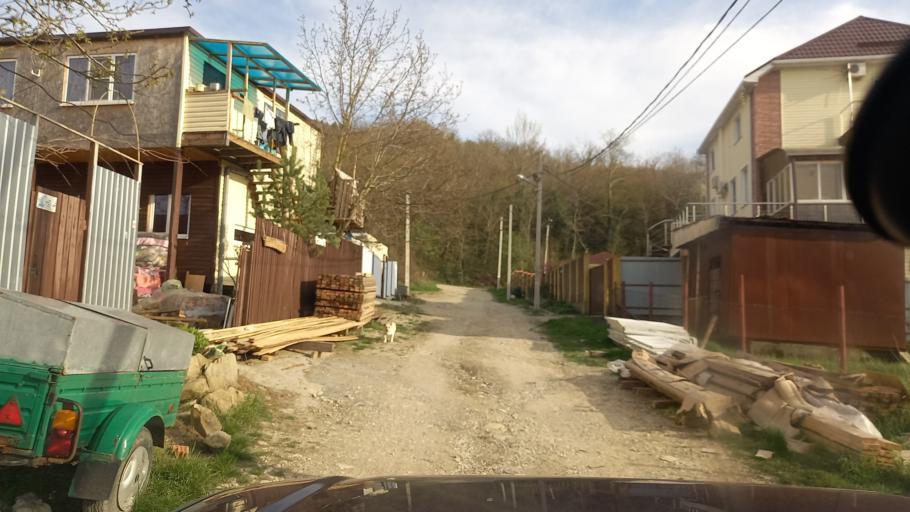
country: RU
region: Krasnodarskiy
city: Arkhipo-Osipovka
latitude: 44.3666
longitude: 38.5472
